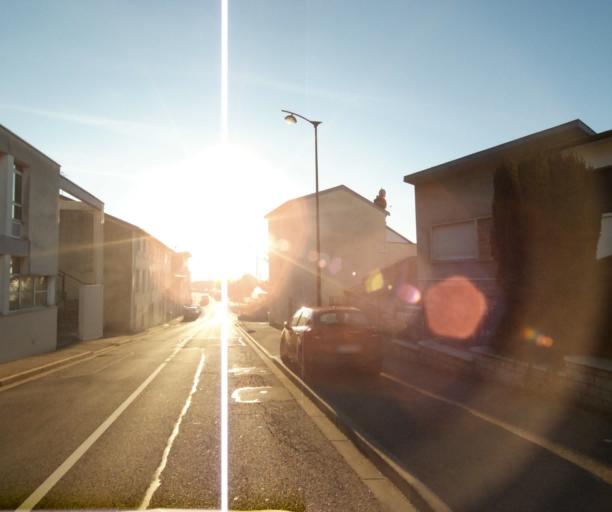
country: FR
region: Lorraine
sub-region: Departement de Meurthe-et-Moselle
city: Laxou
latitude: 48.6879
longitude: 6.1419
